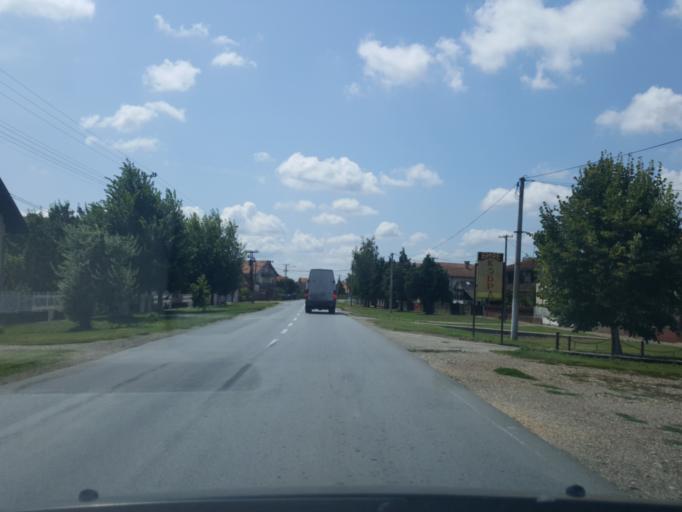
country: RS
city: Salas Nocajski
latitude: 44.9515
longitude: 19.5939
